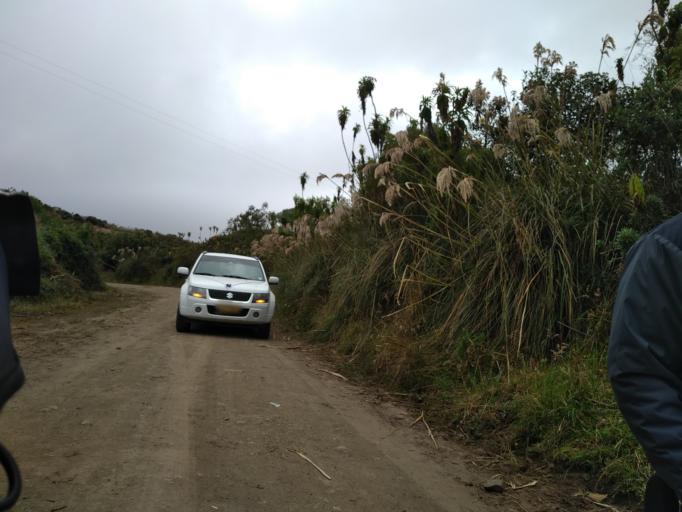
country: EC
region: Carchi
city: Tulcan
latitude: 0.7405
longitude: -77.7890
